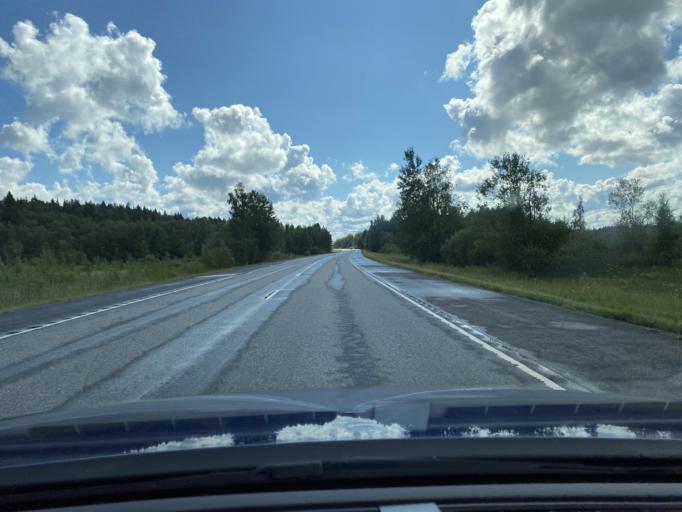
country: FI
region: Pirkanmaa
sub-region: Tampere
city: Lempaeaelae
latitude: 61.3383
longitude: 23.7852
